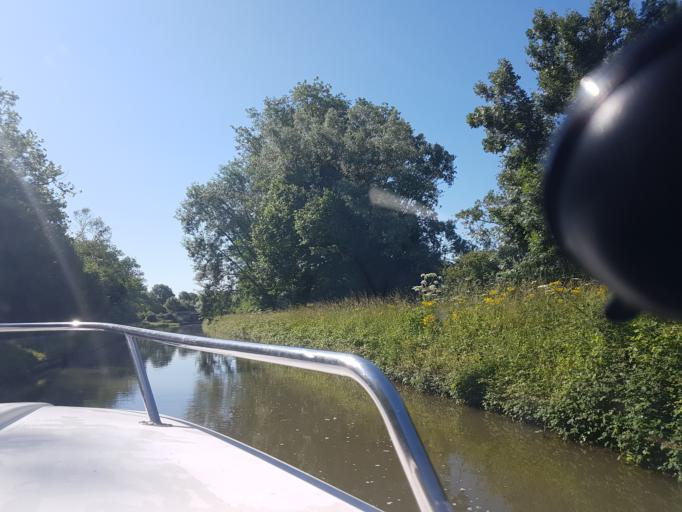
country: FR
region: Bourgogne
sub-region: Departement de la Nievre
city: Clamecy
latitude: 47.5336
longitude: 3.6006
